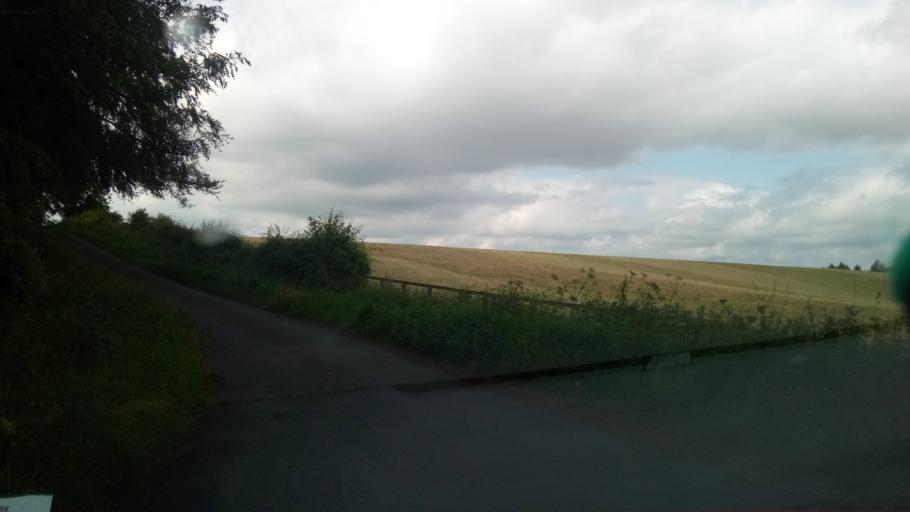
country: GB
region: Scotland
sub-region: The Scottish Borders
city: Hawick
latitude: 55.4387
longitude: -2.6937
